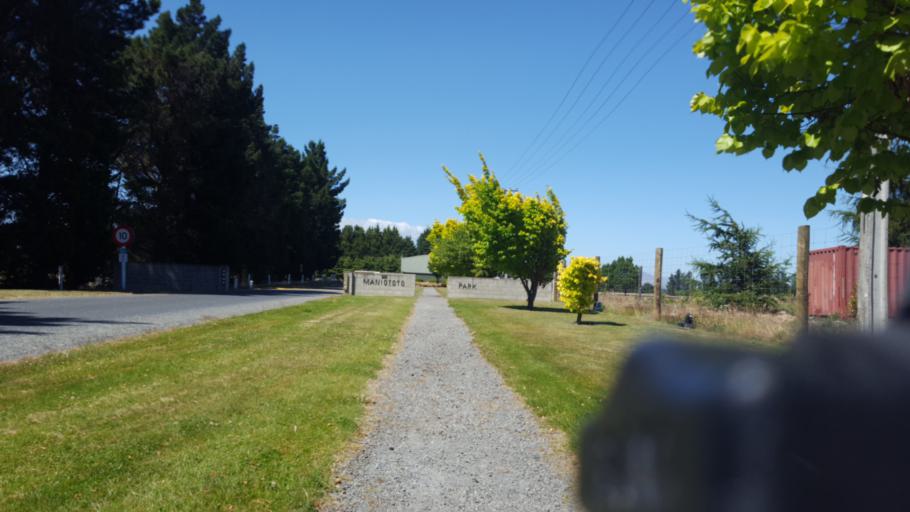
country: NZ
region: Otago
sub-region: Dunedin City
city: Dunedin
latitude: -45.1308
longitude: 170.1059
